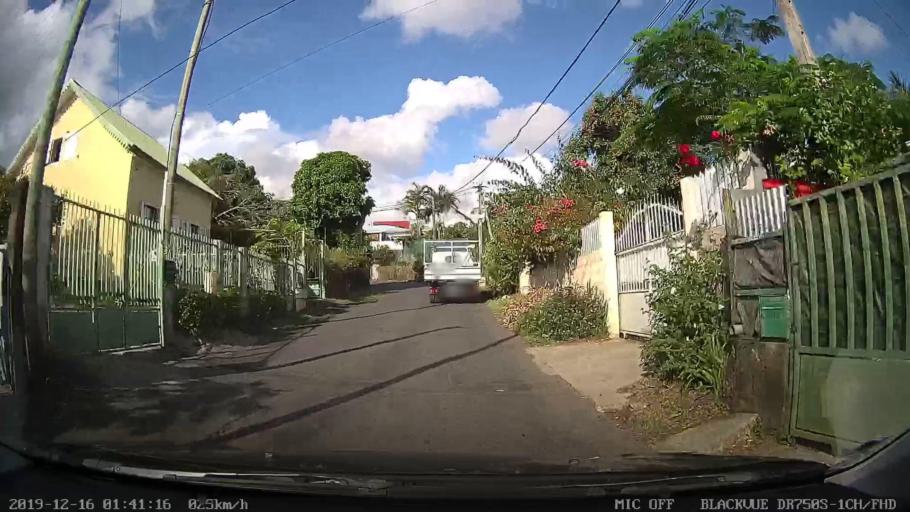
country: RE
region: Reunion
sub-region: Reunion
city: Le Tampon
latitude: -21.2564
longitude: 55.5083
